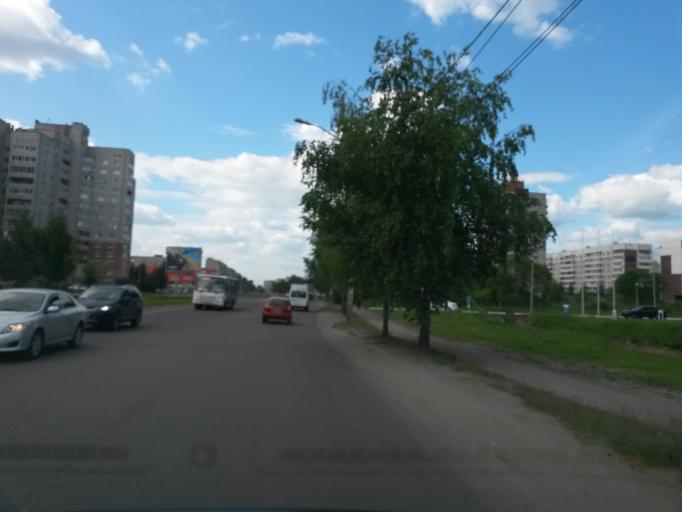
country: RU
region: Jaroslavl
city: Yaroslavl
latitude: 57.6432
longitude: 39.9580
